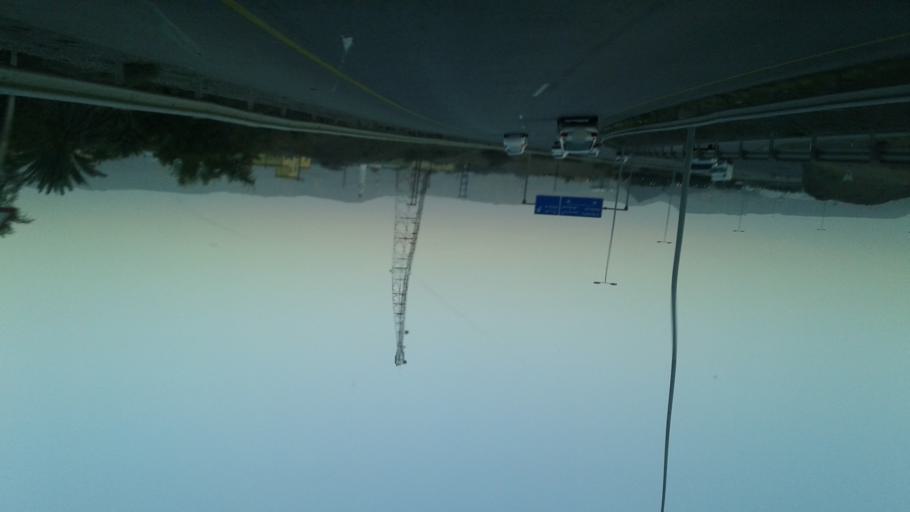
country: OM
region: Muhafazat ad Dakhiliyah
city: Bidbid
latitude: 23.4801
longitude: 58.1988
